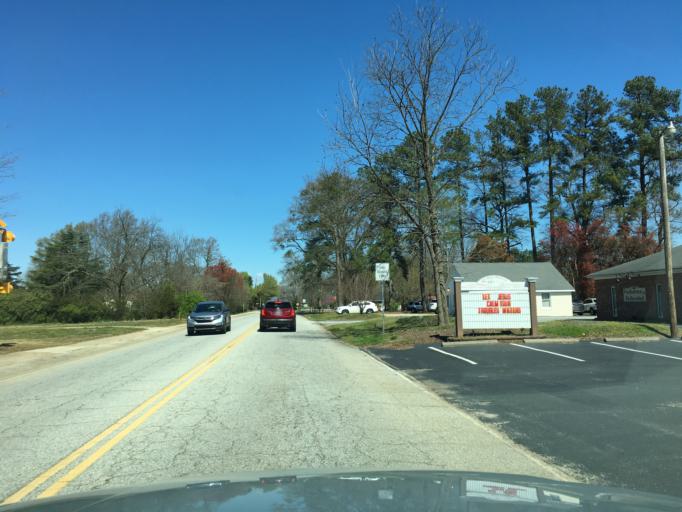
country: US
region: South Carolina
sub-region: Spartanburg County
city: Fairforest
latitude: 34.9274
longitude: -82.0013
